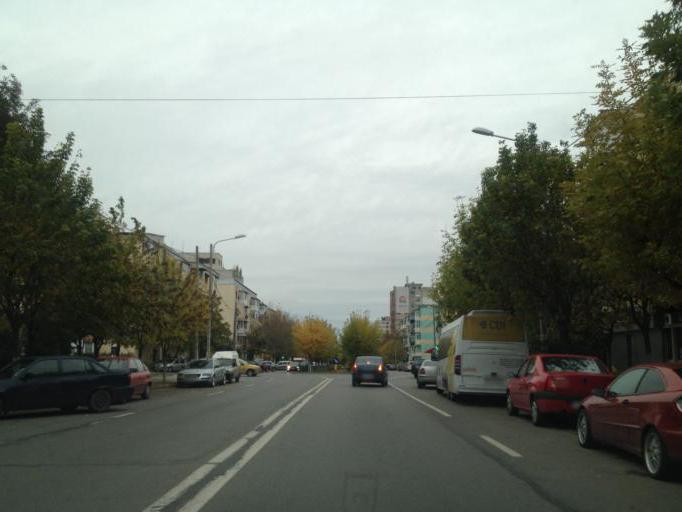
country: RO
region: Dolj
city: Craiova
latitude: 44.3321
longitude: 23.7820
